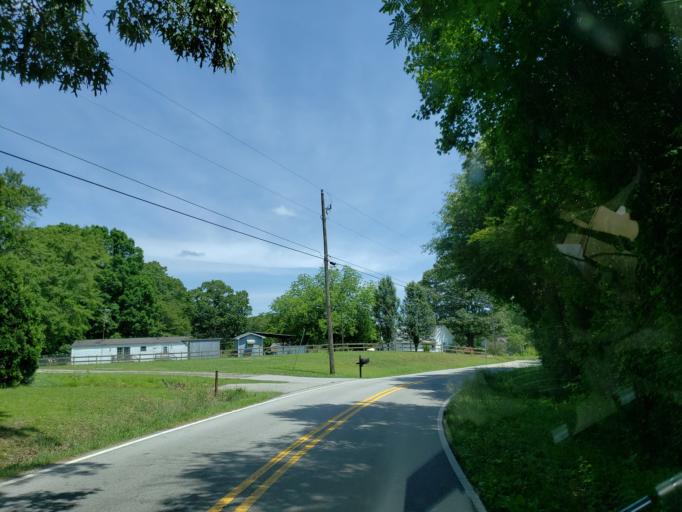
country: US
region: Georgia
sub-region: Paulding County
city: Hiram
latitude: 33.9020
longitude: -84.7643
